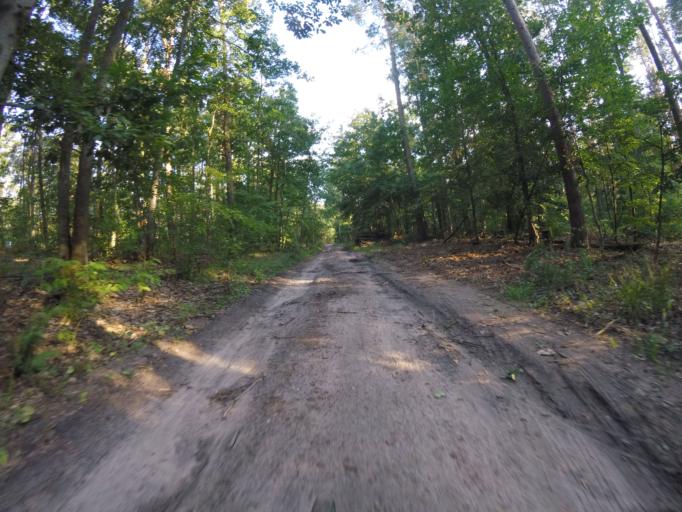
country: DE
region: Brandenburg
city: Petershagen
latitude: 52.5697
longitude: 13.8229
